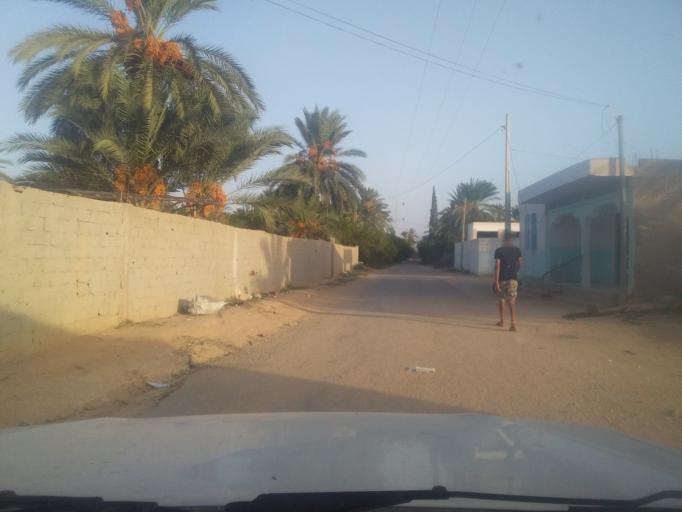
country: TN
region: Qabis
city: Gabes
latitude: 33.6210
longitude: 10.2967
